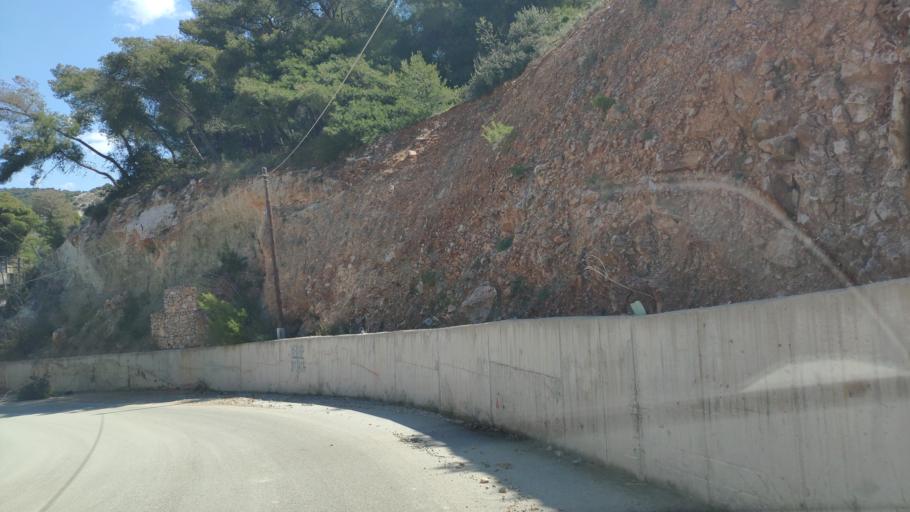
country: GR
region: Attica
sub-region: Nomarchia Athinas
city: Chaidari
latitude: 38.0311
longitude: 23.6340
